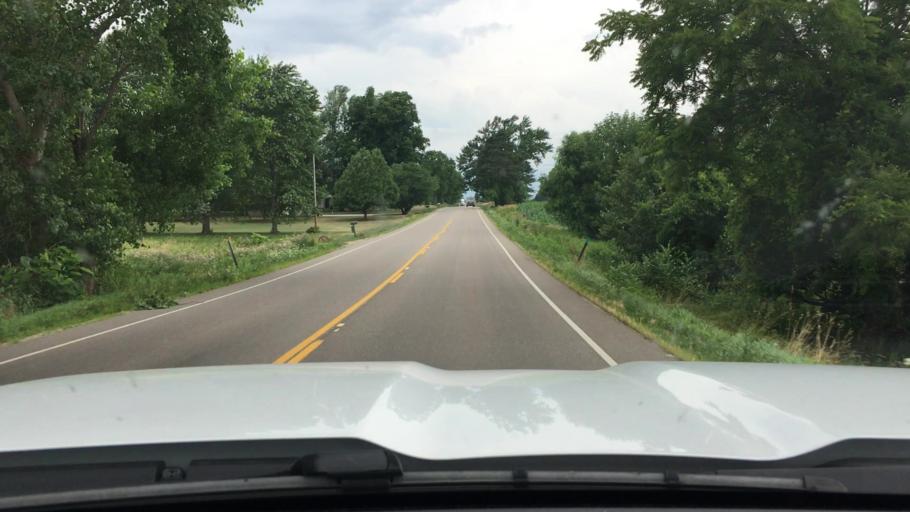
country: US
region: Michigan
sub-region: Kent County
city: Byron Center
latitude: 42.7825
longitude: -85.8098
